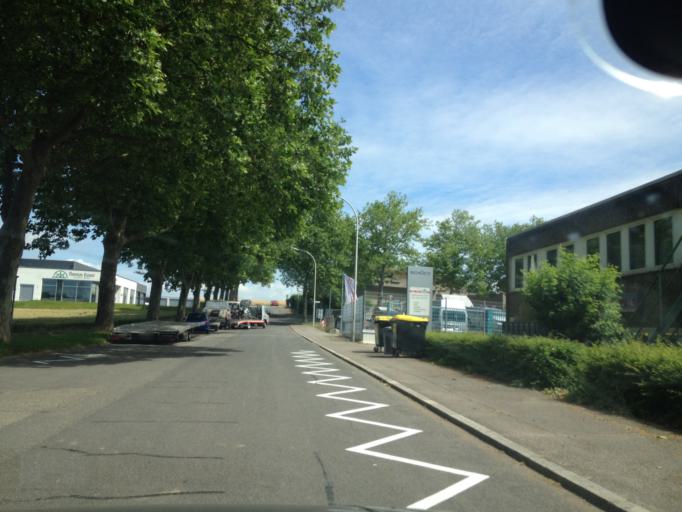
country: DE
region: Baden-Wuerttemberg
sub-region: Regierungsbezirk Stuttgart
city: Leingarten
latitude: 49.1422
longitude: 9.1597
